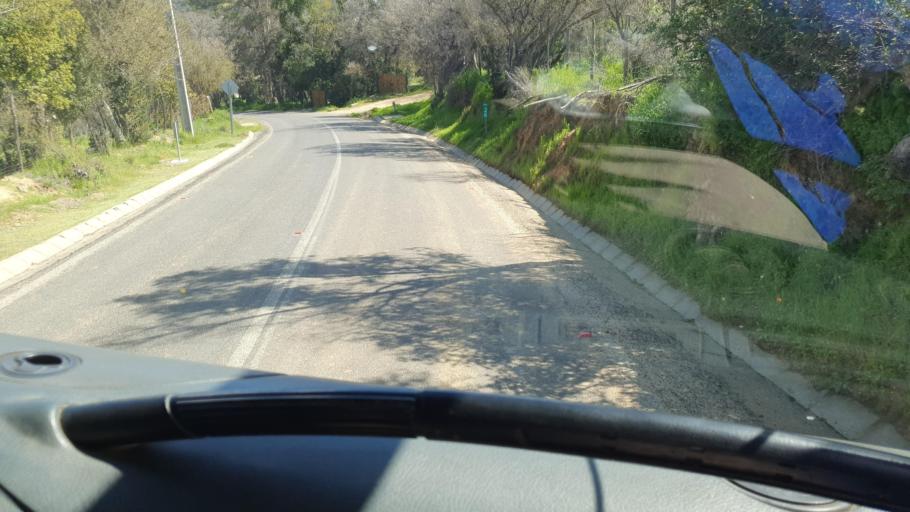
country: CL
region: Valparaiso
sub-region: Provincia de Marga Marga
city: Limache
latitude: -33.1712
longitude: -71.1638
